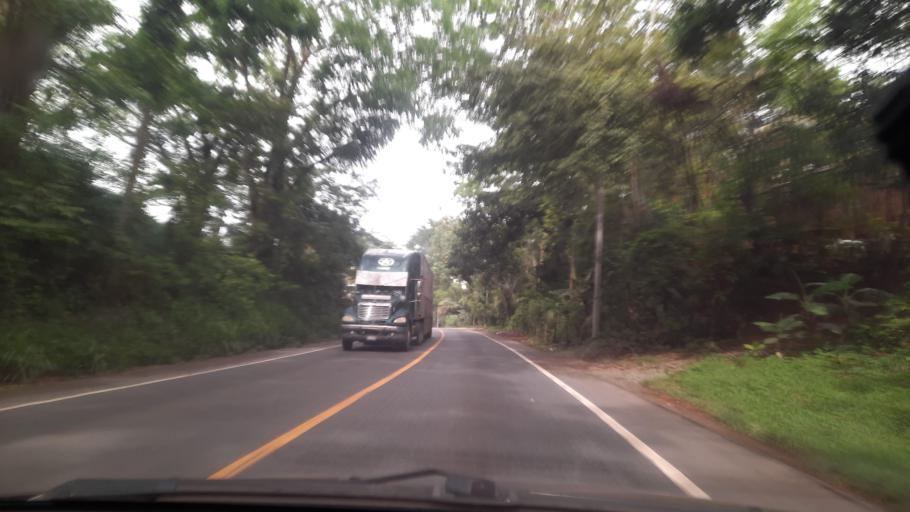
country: GT
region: Izabal
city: Morales
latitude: 15.5103
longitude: -88.8061
